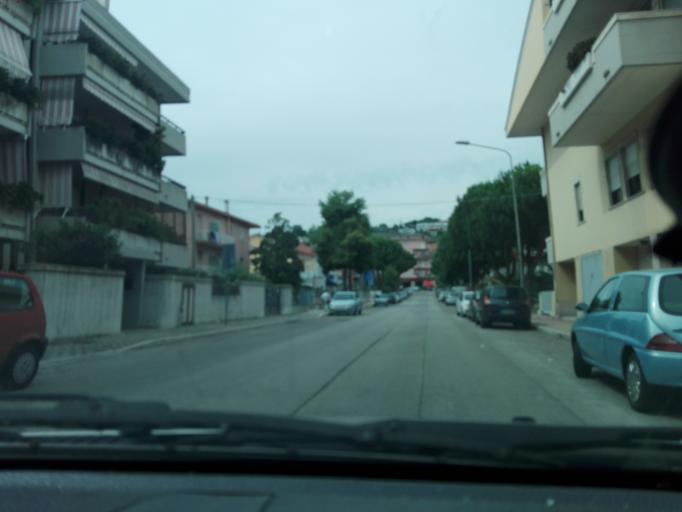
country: IT
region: Abruzzo
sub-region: Provincia di Pescara
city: Montesilvano Marina
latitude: 42.4966
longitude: 14.1735
